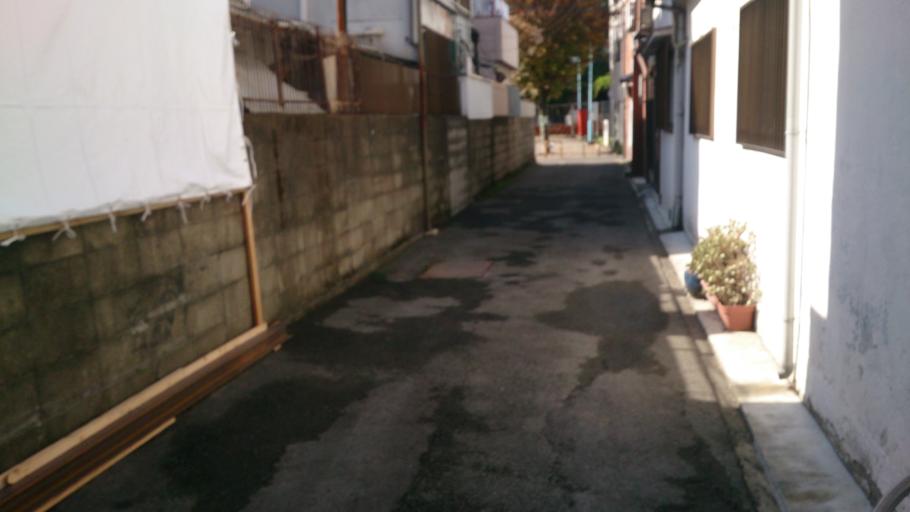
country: JP
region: Osaka
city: Osaka-shi
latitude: 34.7082
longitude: 135.5053
